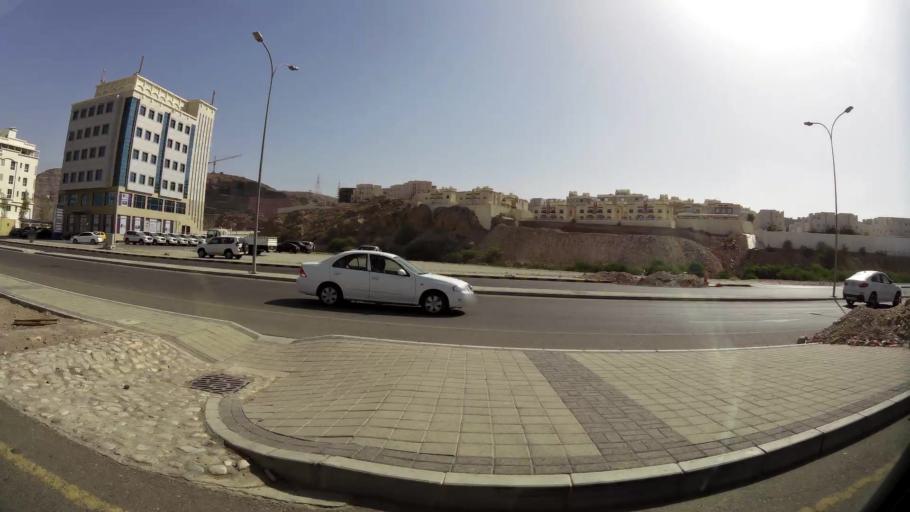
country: OM
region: Muhafazat Masqat
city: Muscat
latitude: 23.6053
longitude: 58.4993
